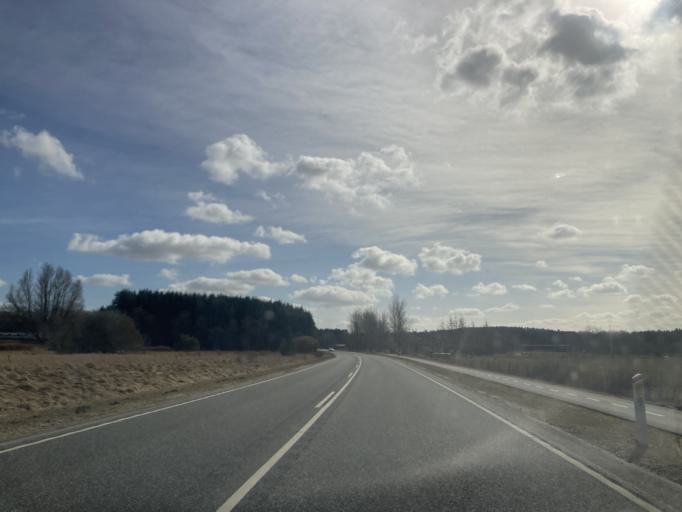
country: DK
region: Central Jutland
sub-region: Hedensted Kommune
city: Torring
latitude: 55.9798
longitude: 9.3935
